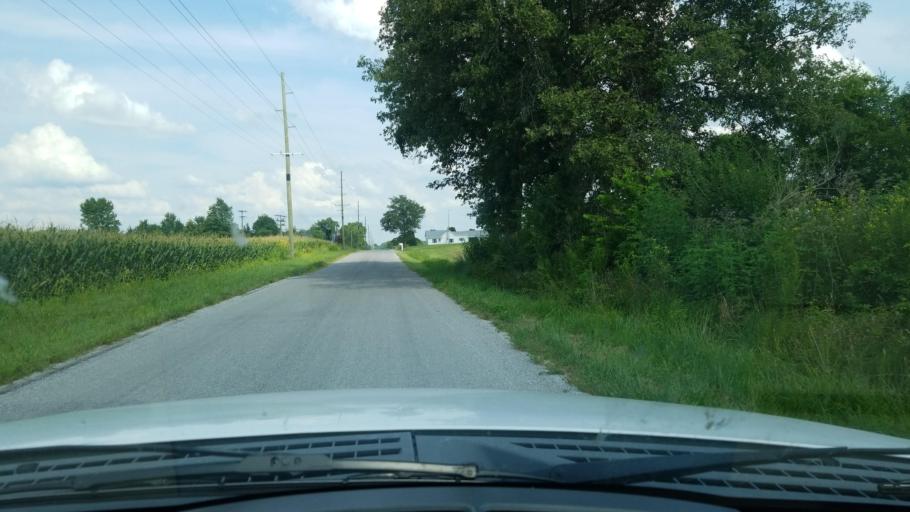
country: US
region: Illinois
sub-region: Saline County
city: Eldorado
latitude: 37.8630
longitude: -88.5145
